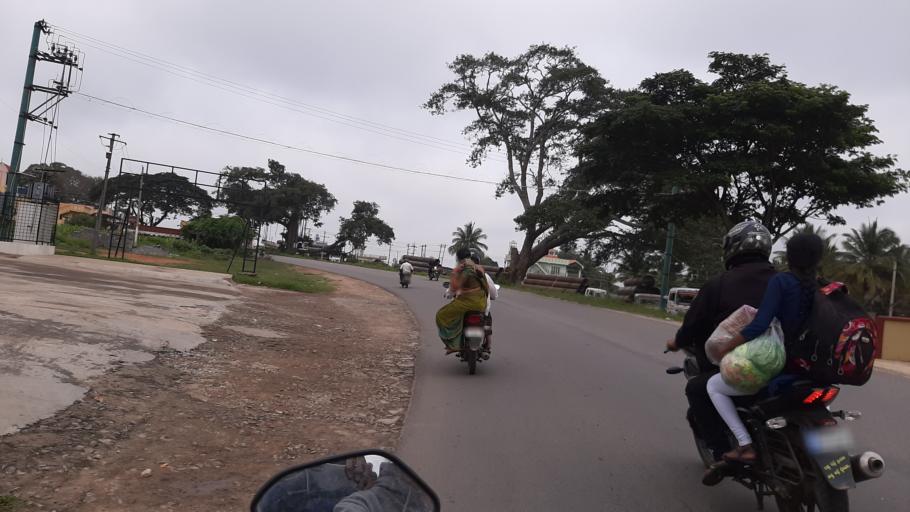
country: IN
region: Karnataka
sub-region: Bangalore Rural
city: Nelamangala
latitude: 12.9675
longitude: 77.3899
